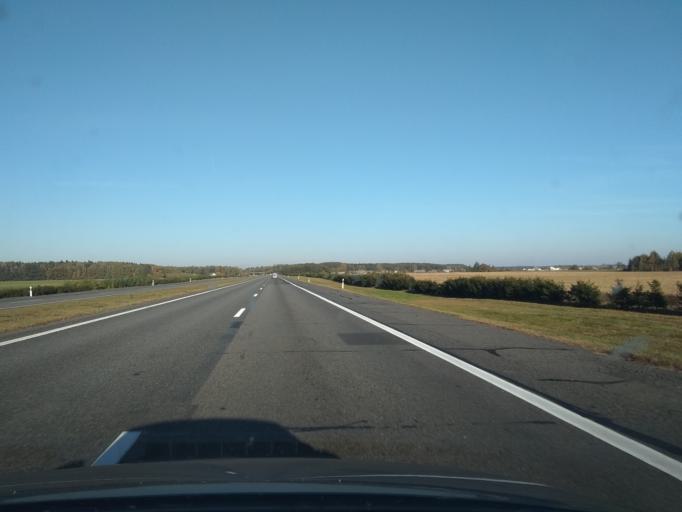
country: BY
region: Brest
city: Ivatsevichy
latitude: 52.6703
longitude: 25.3048
